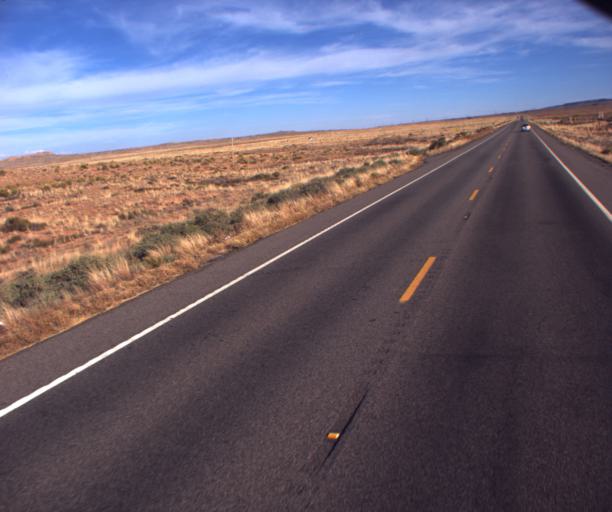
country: US
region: Arizona
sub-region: Apache County
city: Lukachukai
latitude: 36.9451
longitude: -109.2657
